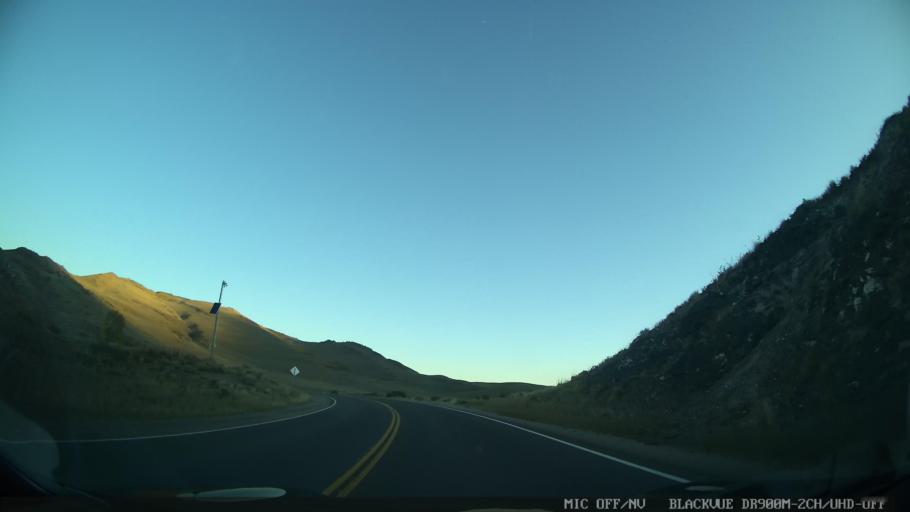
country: US
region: Colorado
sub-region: Eagle County
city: Edwards
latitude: 39.8096
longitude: -106.6741
